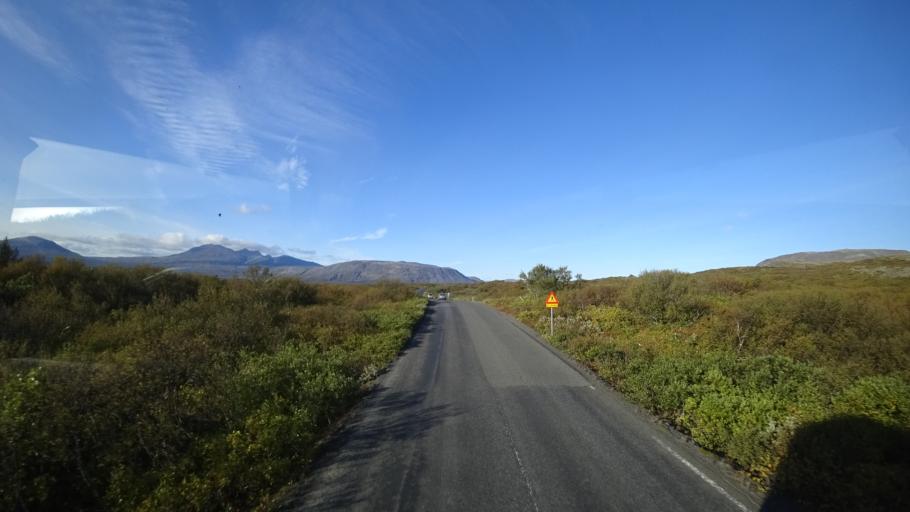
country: IS
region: South
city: Hveragerdi
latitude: 64.2451
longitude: -21.0244
